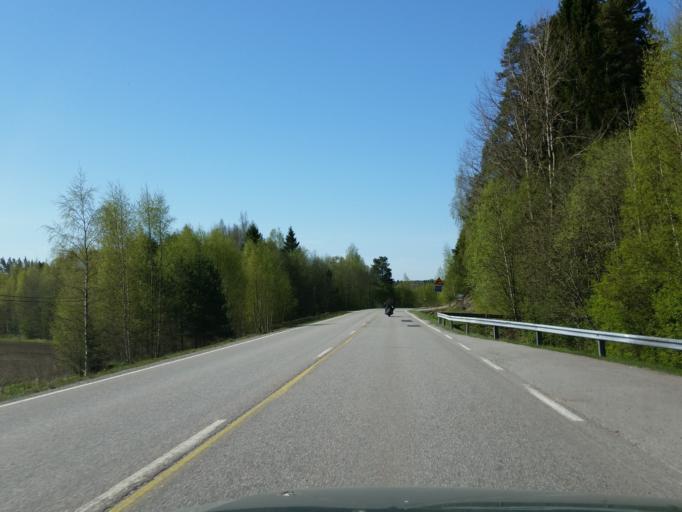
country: FI
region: Uusimaa
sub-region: Helsinki
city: Siuntio
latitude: 60.1806
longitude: 24.2346
